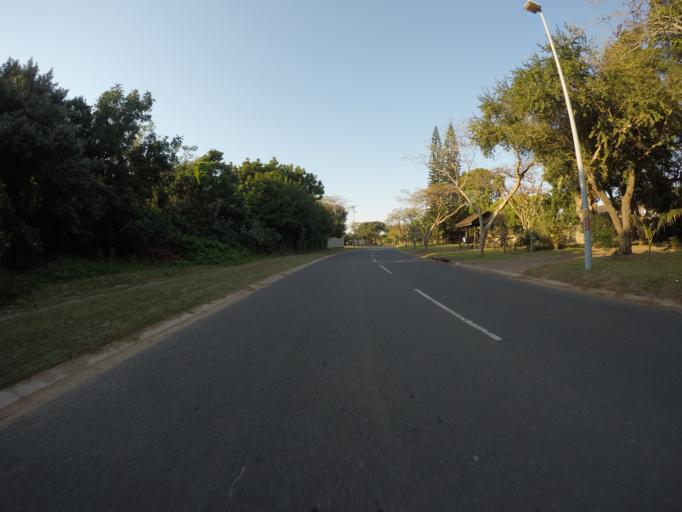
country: ZA
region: KwaZulu-Natal
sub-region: uThungulu District Municipality
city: Richards Bay
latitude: -28.7793
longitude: 32.1108
